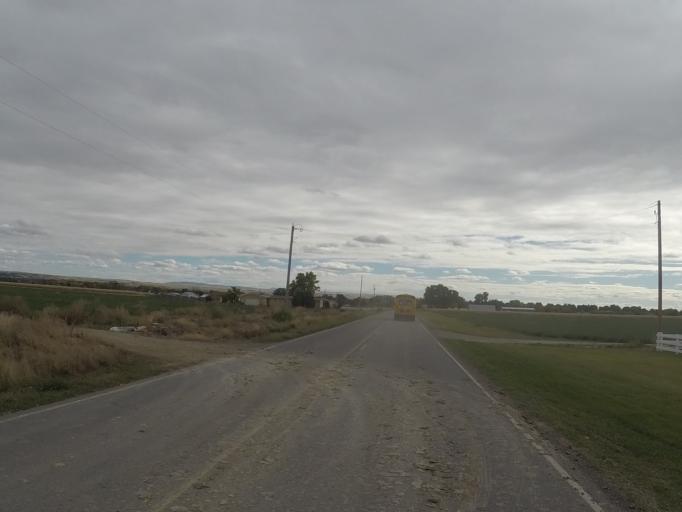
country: US
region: Montana
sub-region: Yellowstone County
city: Laurel
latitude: 45.7468
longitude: -108.6589
